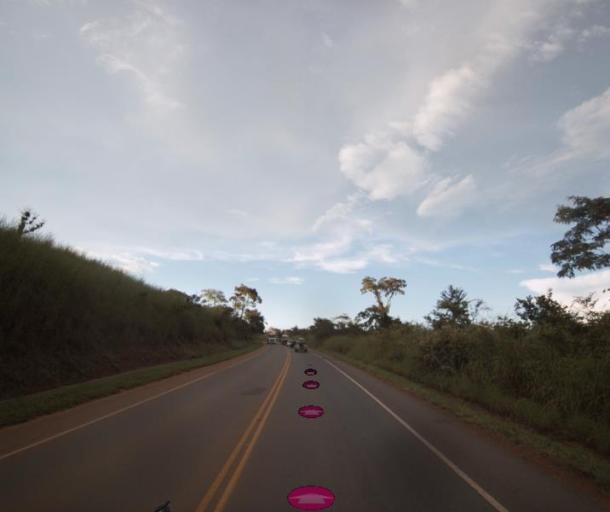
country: BR
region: Goias
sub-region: Anapolis
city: Anapolis
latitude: -16.2324
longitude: -48.9299
